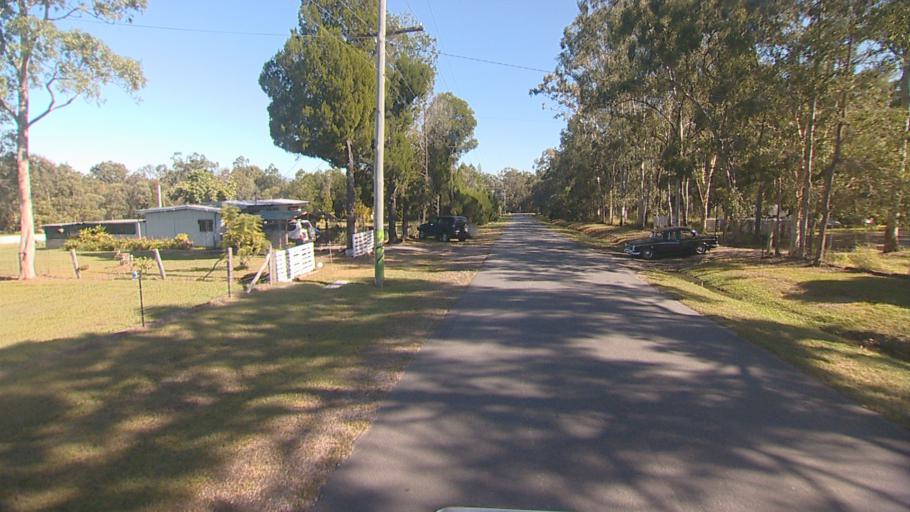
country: AU
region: Queensland
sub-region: Logan
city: Park Ridge South
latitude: -27.6939
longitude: 153.0072
